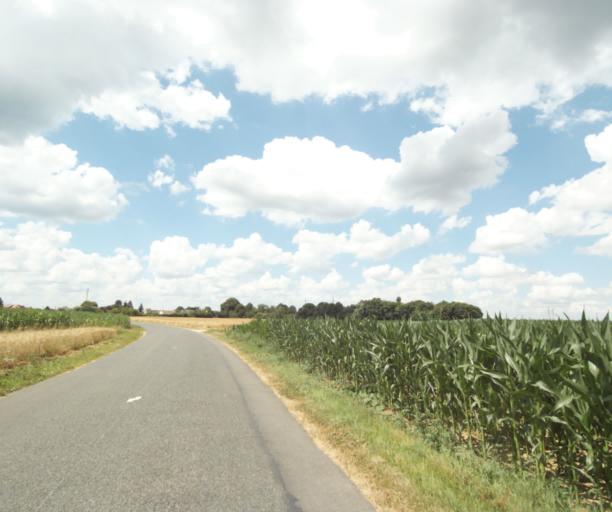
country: FR
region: Ile-de-France
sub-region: Departement de Seine-et-Marne
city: Hericy
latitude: 48.4443
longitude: 2.7834
